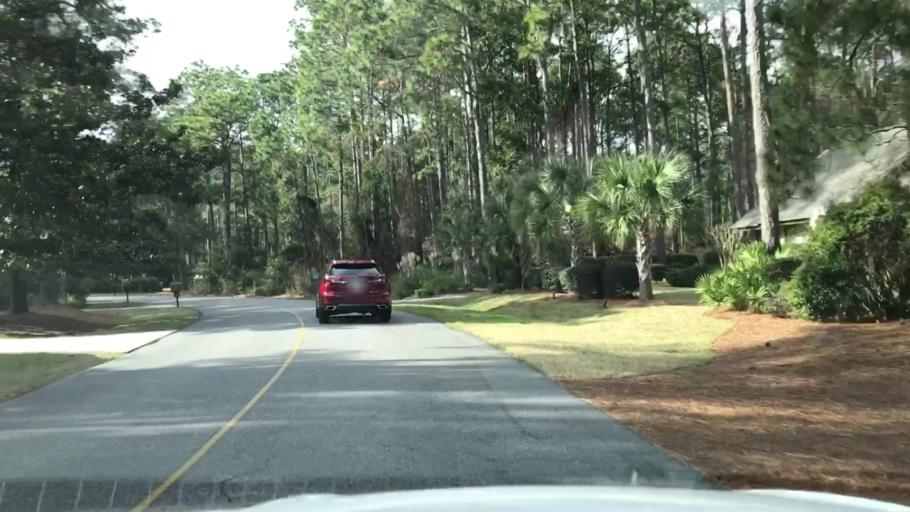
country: US
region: South Carolina
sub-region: Beaufort County
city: Hilton Head Island
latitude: 32.2407
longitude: -80.7164
